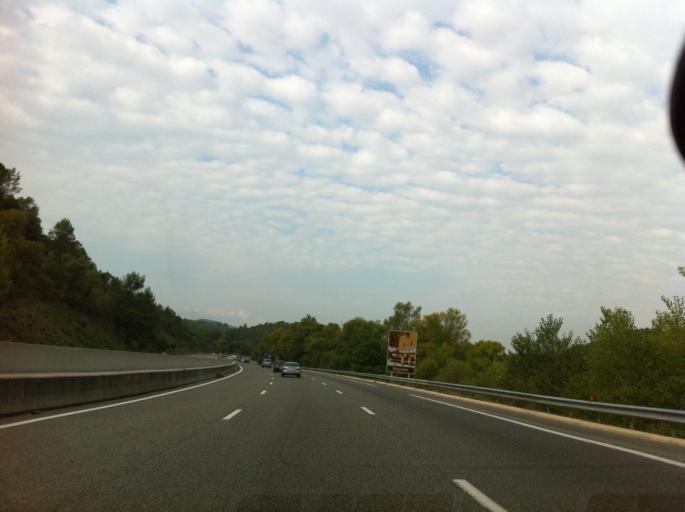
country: FR
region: Provence-Alpes-Cote d'Azur
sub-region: Departement du Var
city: Camps-la-Source
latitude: 43.4197
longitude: 6.1153
